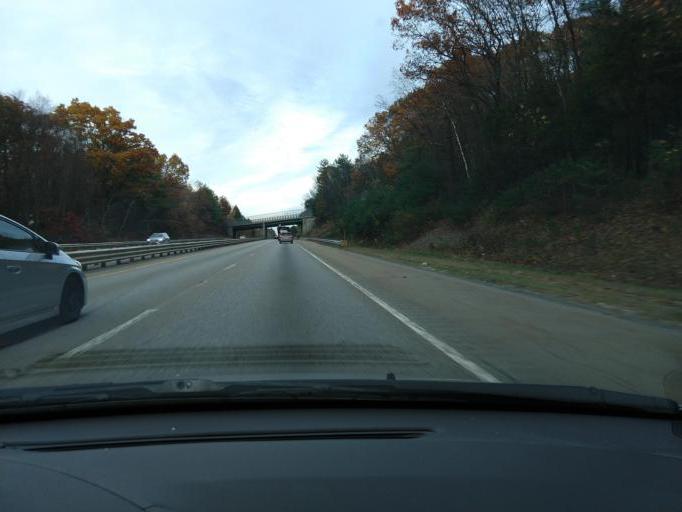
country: US
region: Massachusetts
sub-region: Worcester County
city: Harvard
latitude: 42.5240
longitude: -71.5533
